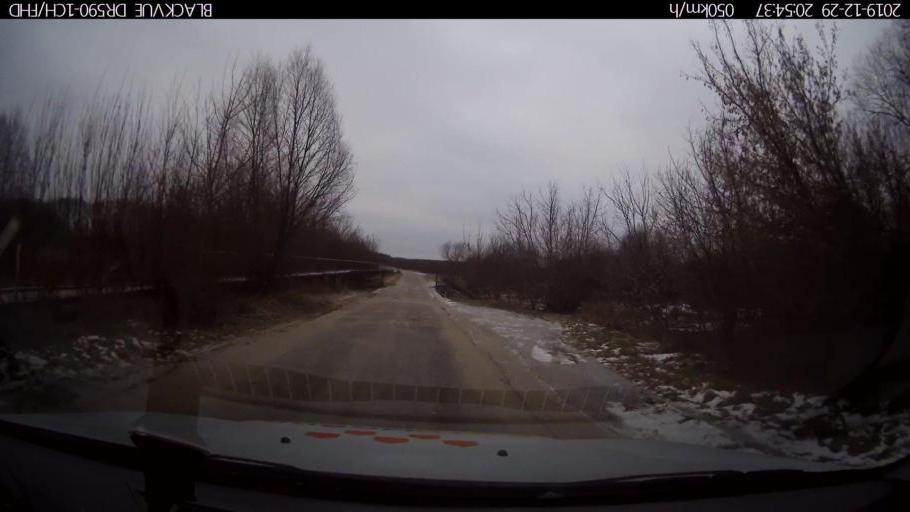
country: RU
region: Nizjnij Novgorod
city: Afonino
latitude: 56.1628
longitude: 43.9907
